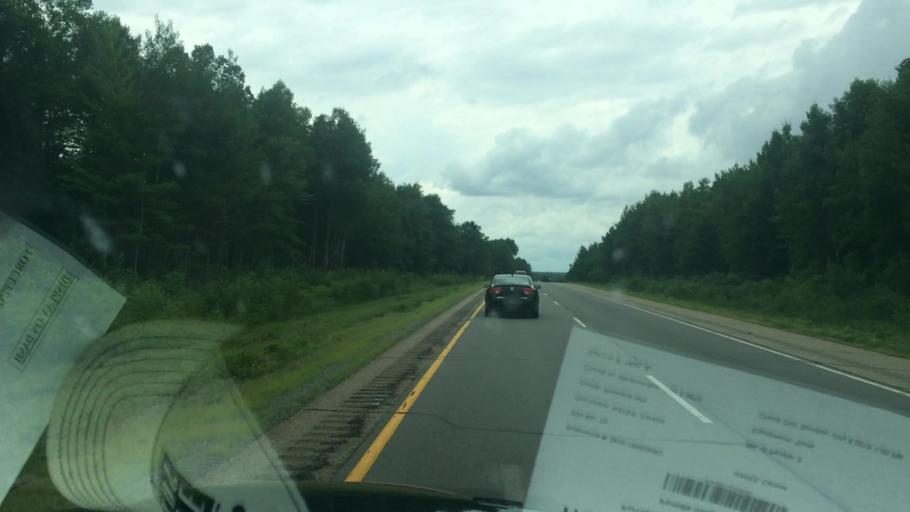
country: US
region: Wisconsin
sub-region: Marathon County
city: Mosinee
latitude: 44.7039
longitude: -89.6526
